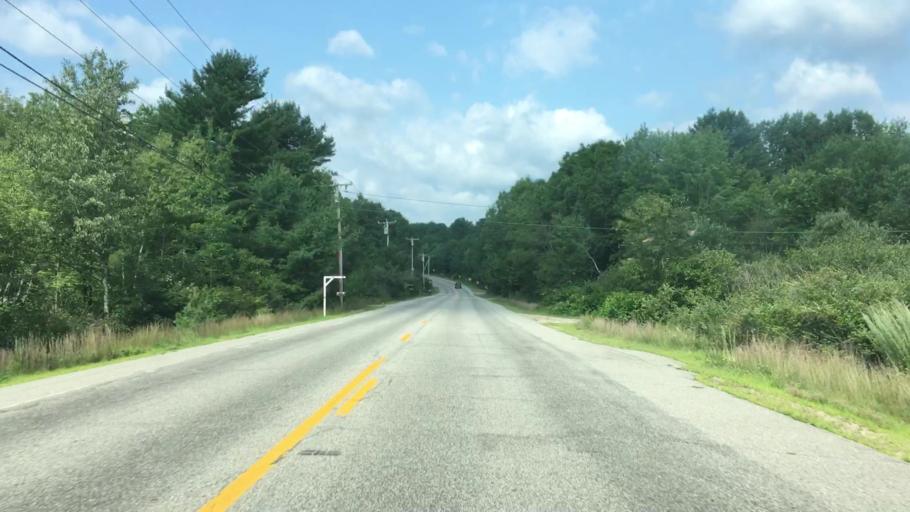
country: US
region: Maine
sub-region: Androscoggin County
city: Minot
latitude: 44.0293
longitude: -70.3333
